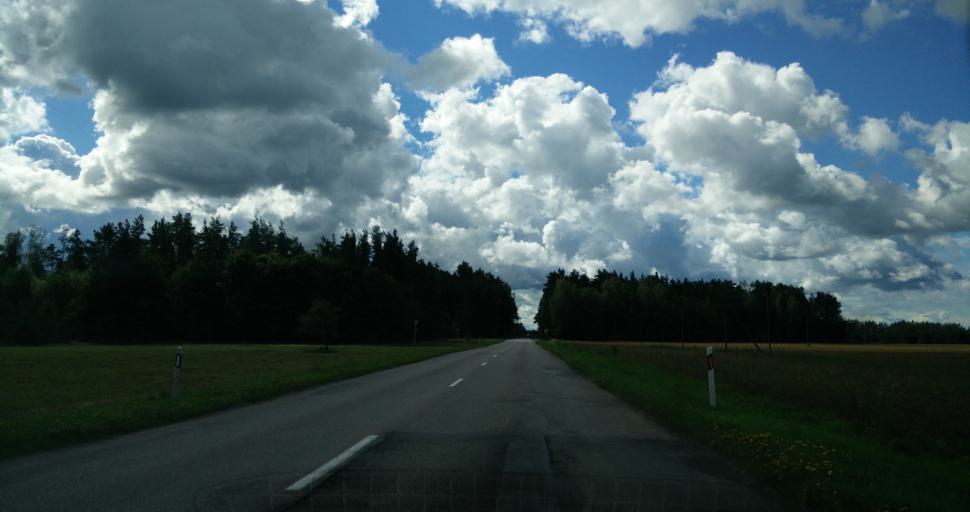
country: LT
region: Klaipedos apskritis
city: Silute
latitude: 55.4472
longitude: 21.4889
